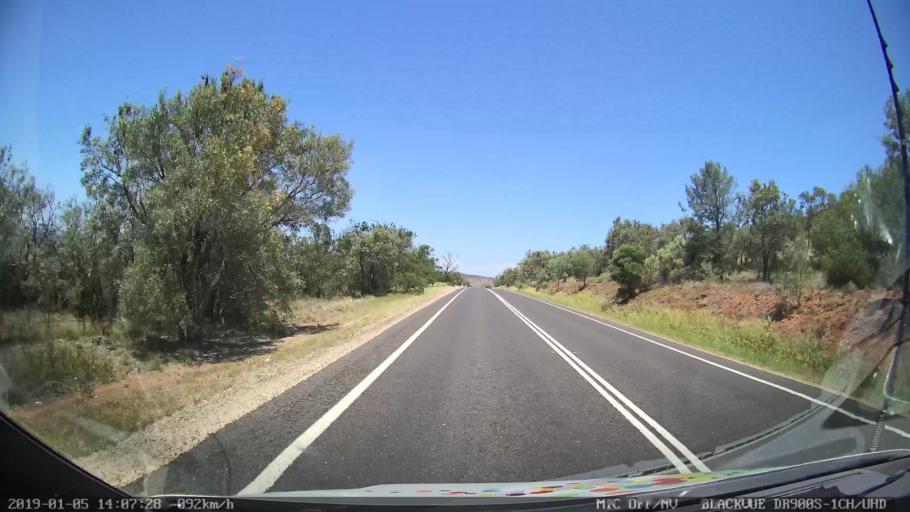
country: AU
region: New South Wales
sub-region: Gunnedah
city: Gunnedah
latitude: -31.2228
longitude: 150.4069
